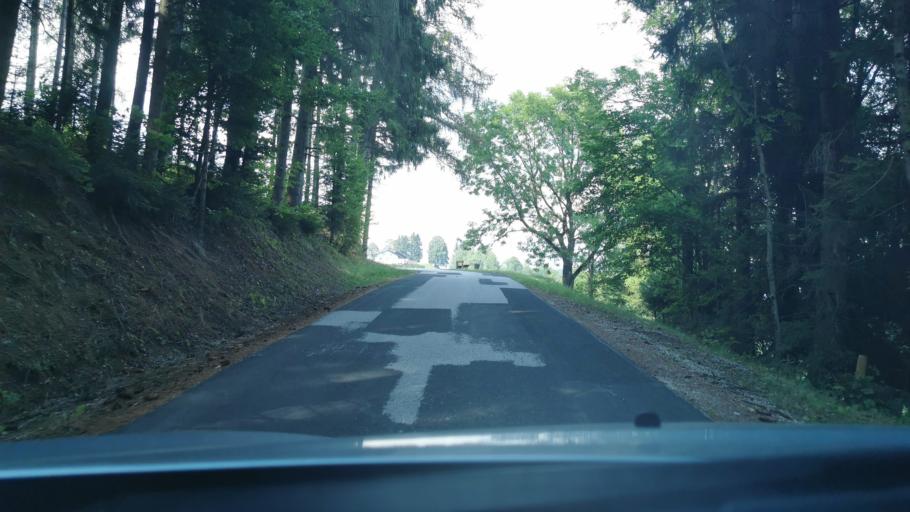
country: AT
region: Styria
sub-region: Politischer Bezirk Weiz
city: Strallegg
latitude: 47.4051
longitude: 15.6903
